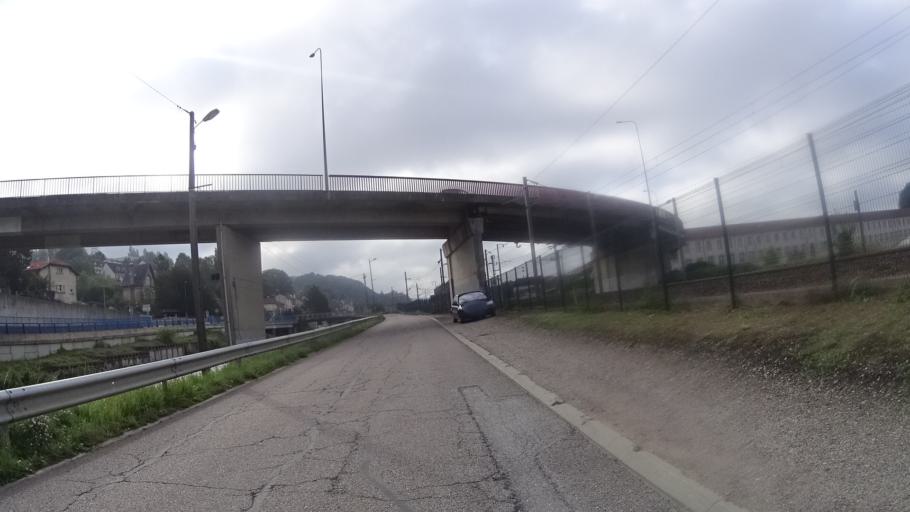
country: FR
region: Lorraine
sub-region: Departement de la Meuse
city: Bar-le-Duc
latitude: 48.7799
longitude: 5.1580
